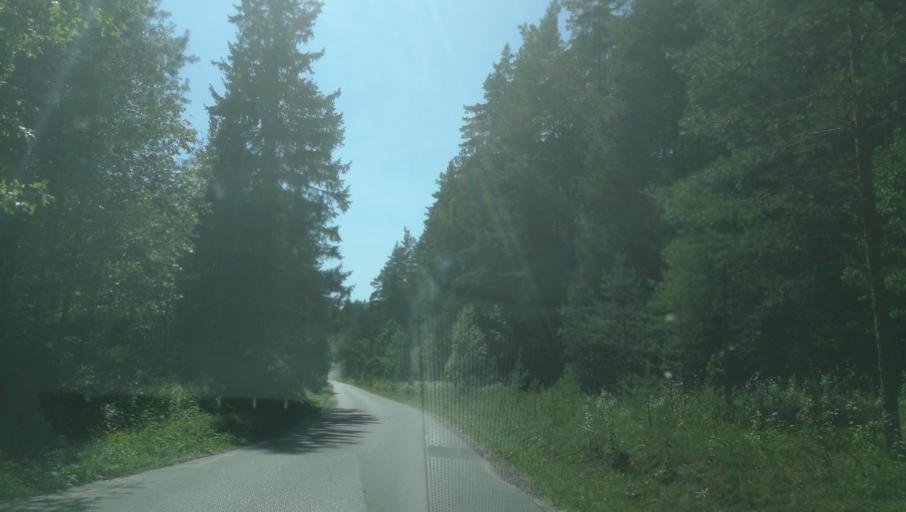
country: LV
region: Cesu Rajons
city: Cesis
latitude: 57.2845
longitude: 25.2140
